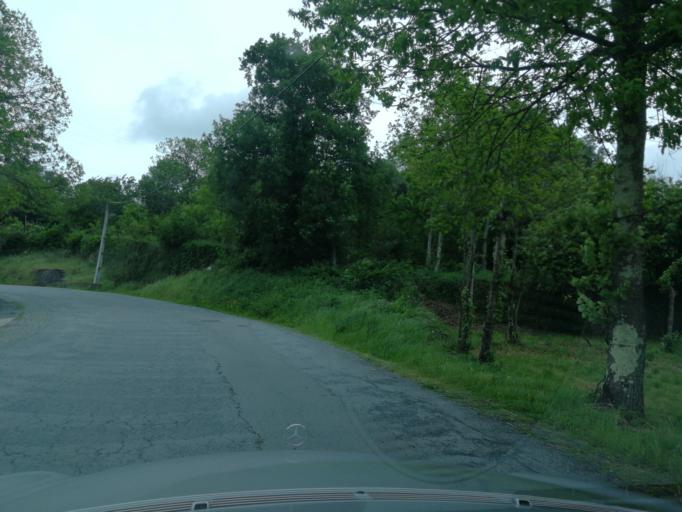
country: PT
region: Braga
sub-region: Braga
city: Adaufe
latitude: 41.6023
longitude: -8.4087
